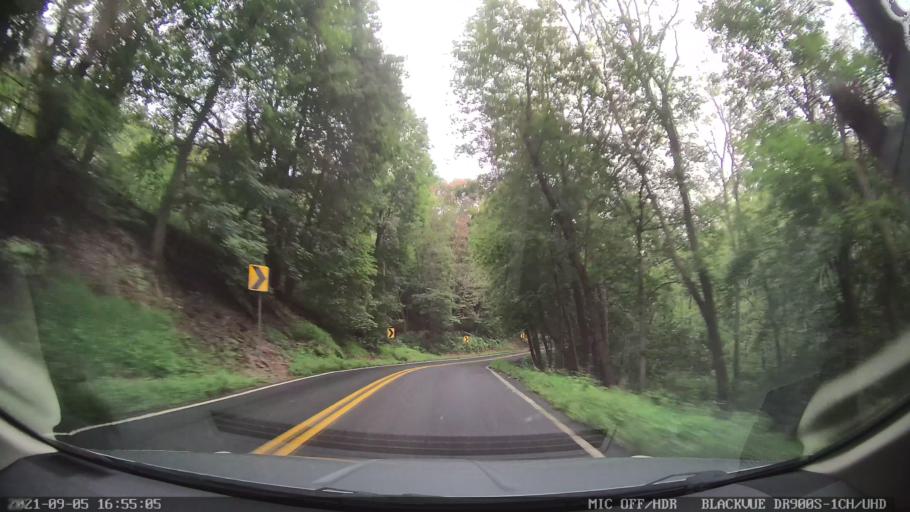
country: US
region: Pennsylvania
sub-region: Lehigh County
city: Wescosville
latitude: 40.6124
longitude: -75.5846
